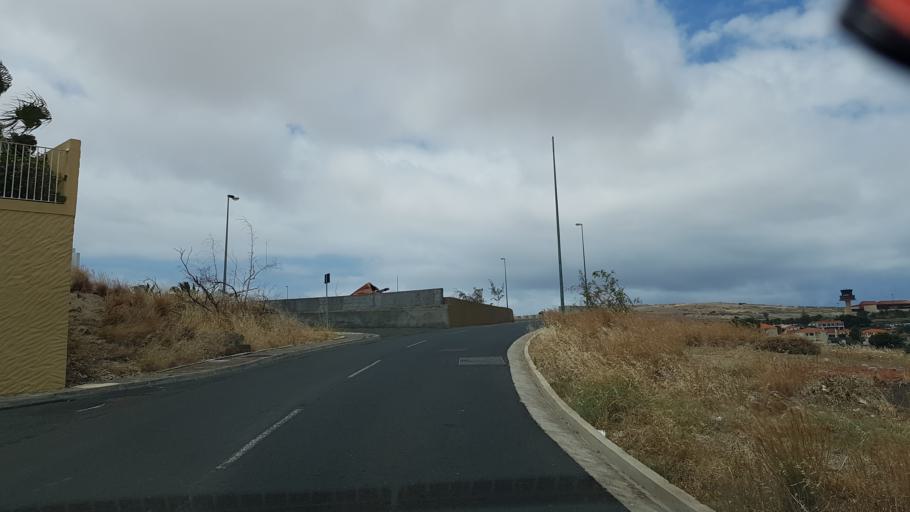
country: PT
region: Madeira
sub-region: Porto Santo
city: Vila de Porto Santo
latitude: 33.0640
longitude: -16.3375
